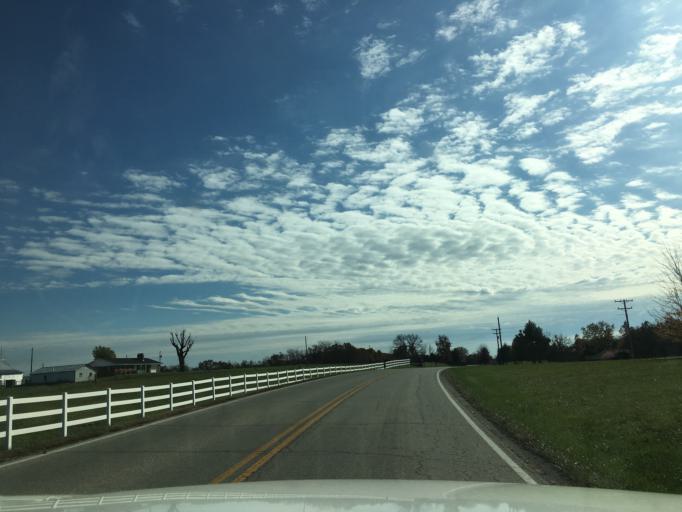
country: US
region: Missouri
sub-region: Osage County
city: Linn
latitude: 38.4334
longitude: -91.8277
